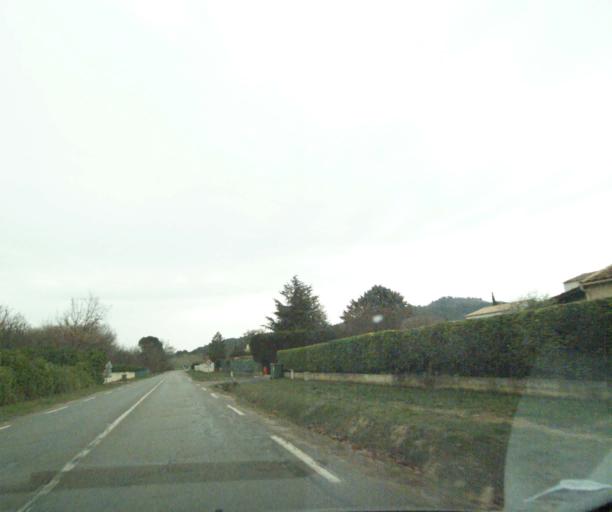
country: FR
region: Provence-Alpes-Cote d'Azur
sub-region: Departement des Bouches-du-Rhone
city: Le Puy-Sainte-Reparade
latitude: 43.6588
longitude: 5.4153
